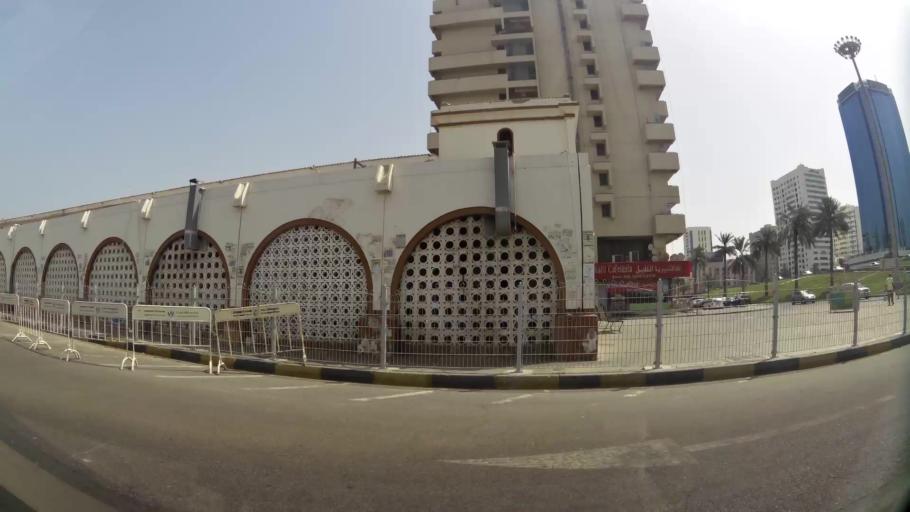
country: AE
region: Ash Shariqah
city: Sharjah
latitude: 25.3515
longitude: 55.3832
